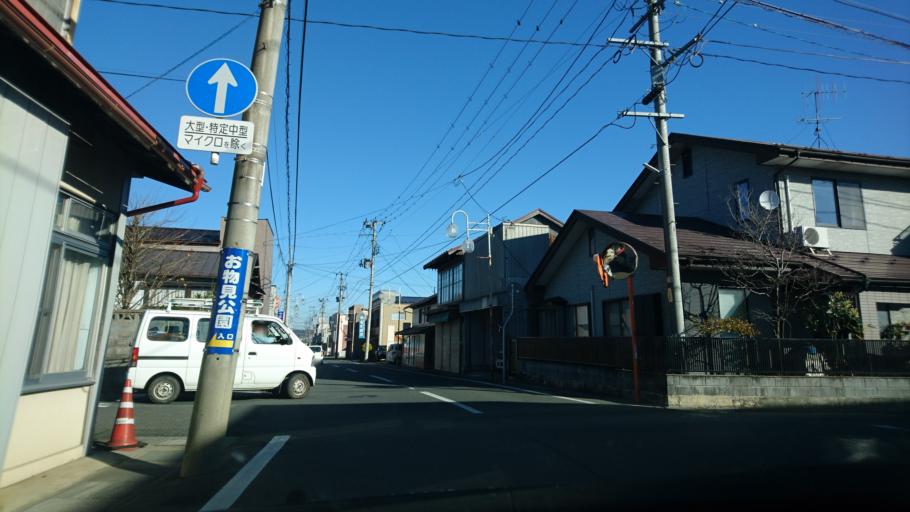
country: JP
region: Iwate
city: Mizusawa
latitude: 39.0466
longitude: 141.1223
